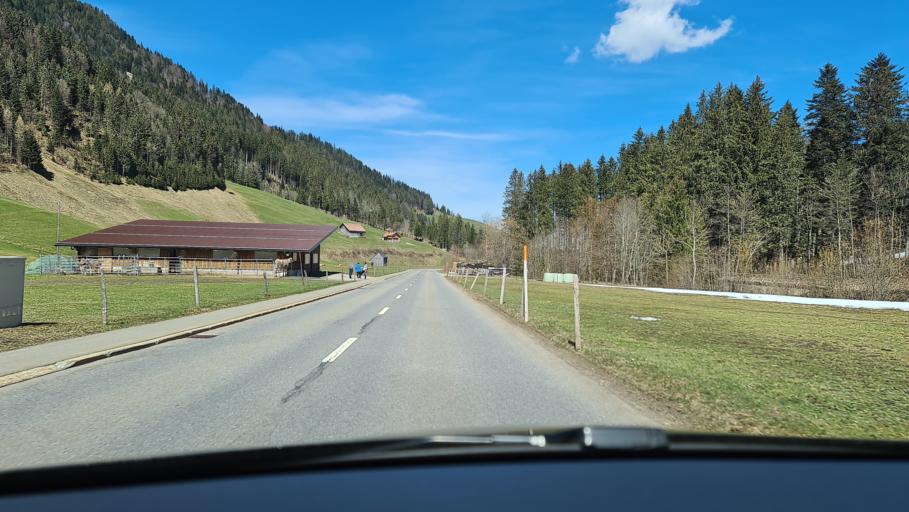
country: CH
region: Schwyz
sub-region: Bezirk Schwyz
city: Rothenthurm
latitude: 47.0574
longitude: 8.7112
